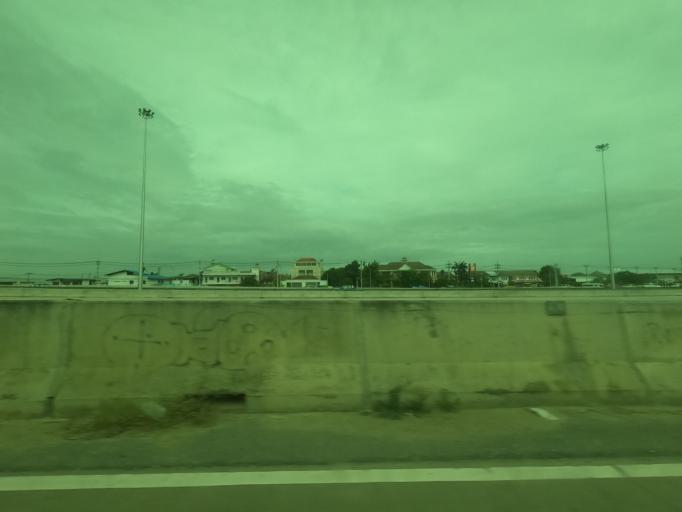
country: TH
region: Nonthaburi
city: Bang Bua Thong
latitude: 13.9365
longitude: 100.4173
